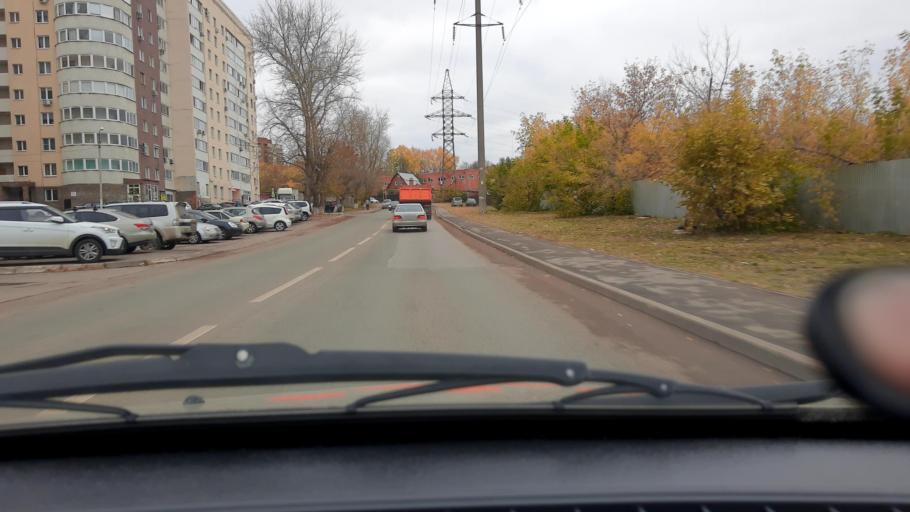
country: RU
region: Bashkortostan
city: Ufa
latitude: 54.7086
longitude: 55.9912
